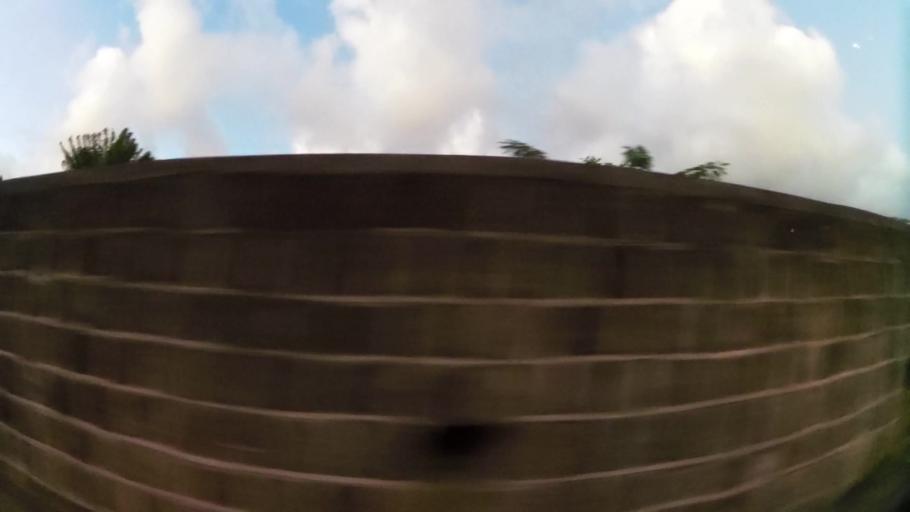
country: KN
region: Saint Thomas Middle Island
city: Middle Island
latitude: 17.3212
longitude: -62.8019
